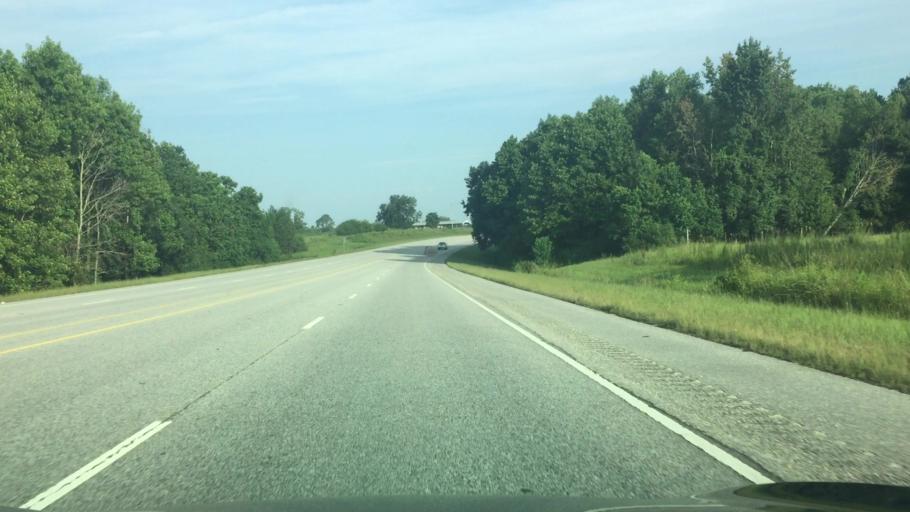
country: US
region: Alabama
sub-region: Butler County
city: Georgiana
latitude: 31.5182
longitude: -86.7100
